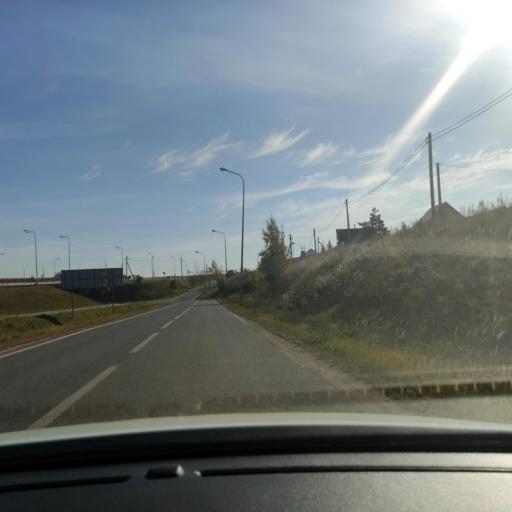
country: RU
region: Tatarstan
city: Vysokaya Gora
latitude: 55.7459
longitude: 49.3955
